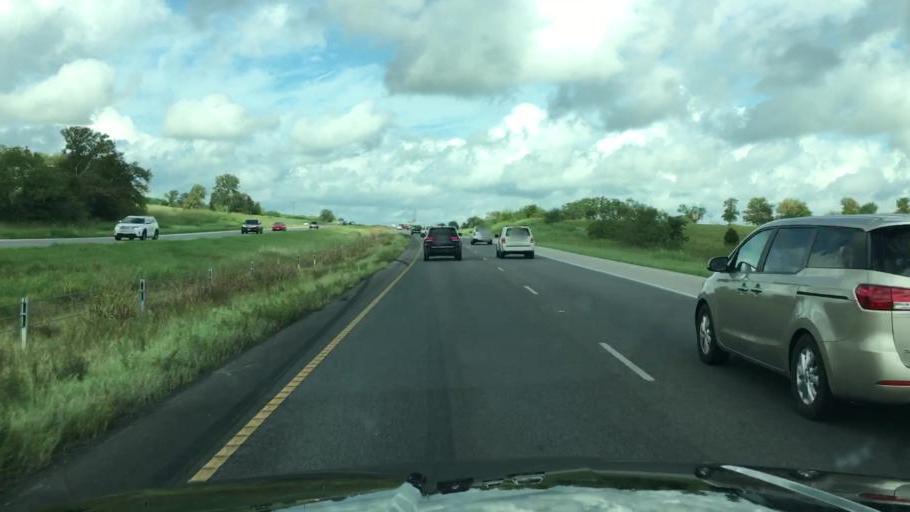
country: US
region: Texas
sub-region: Travis County
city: Garfield
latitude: 30.1689
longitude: -97.5151
